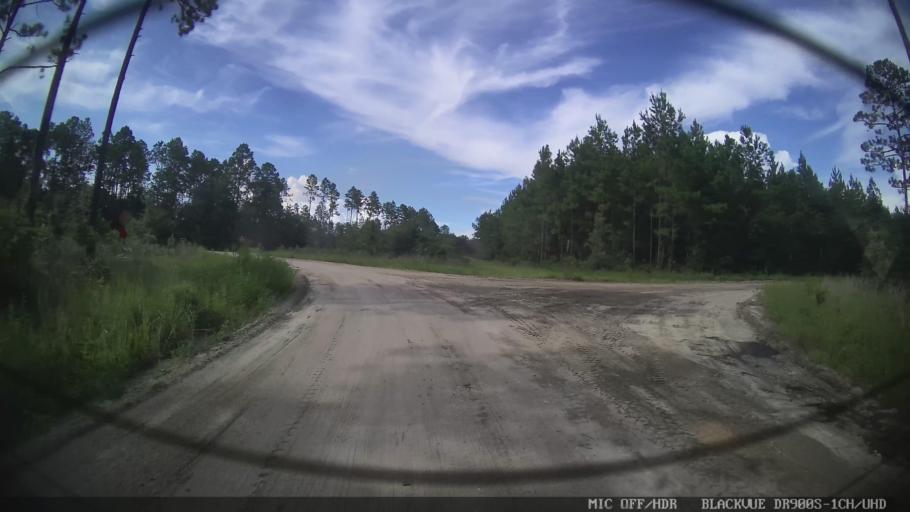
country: US
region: Georgia
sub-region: Echols County
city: Statenville
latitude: 30.6234
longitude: -83.1991
